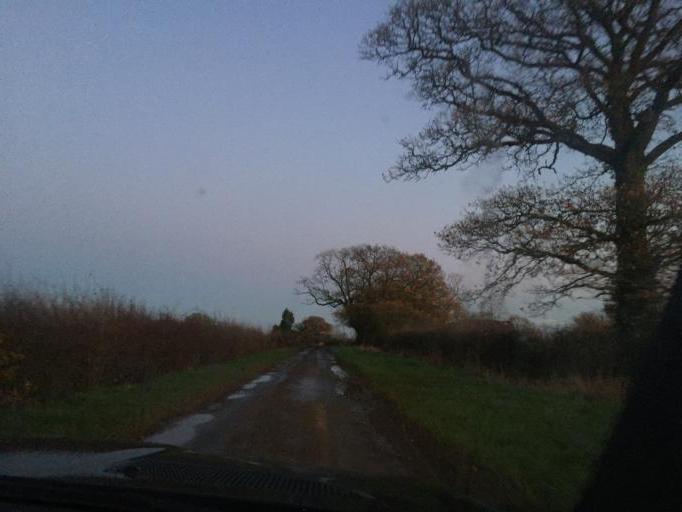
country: GB
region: England
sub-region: Northamptonshire
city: Silverstone
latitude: 52.0889
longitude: -1.0977
